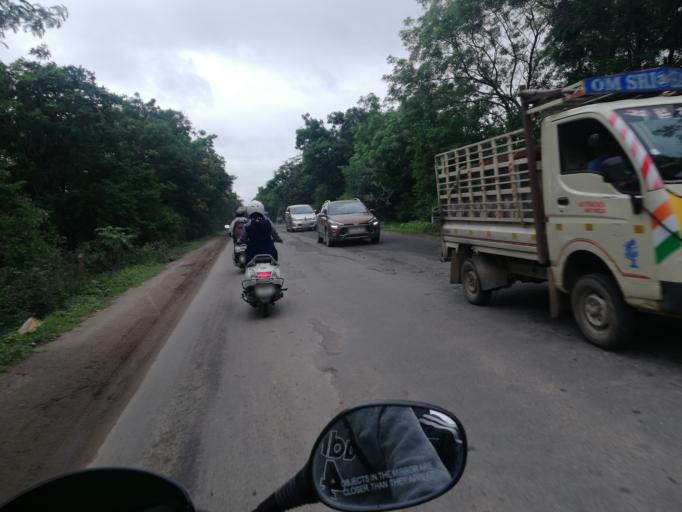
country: IN
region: Telangana
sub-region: Rangareddi
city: Quthbullapur
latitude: 17.5598
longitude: 78.4119
